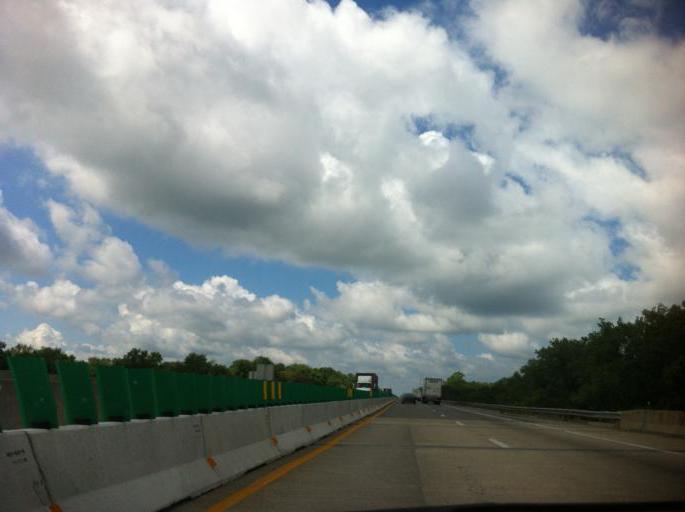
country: US
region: Ohio
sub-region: Lorain County
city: Elyria
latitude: 41.3920
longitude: -82.1254
